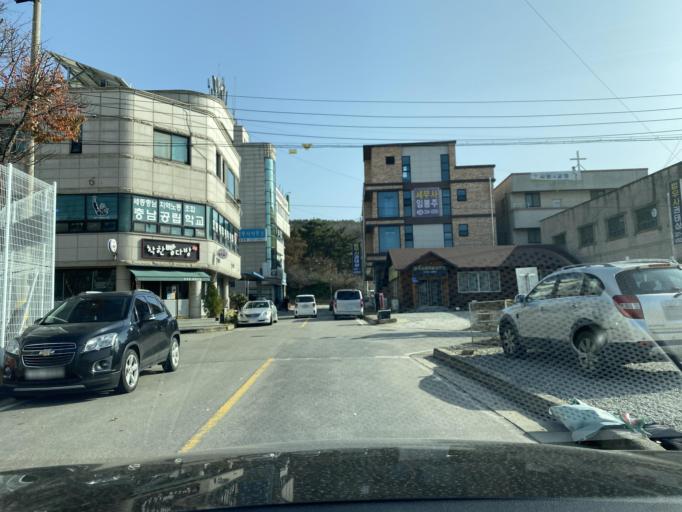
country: KR
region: Chungcheongnam-do
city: Yesan
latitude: 36.6940
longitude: 126.8355
